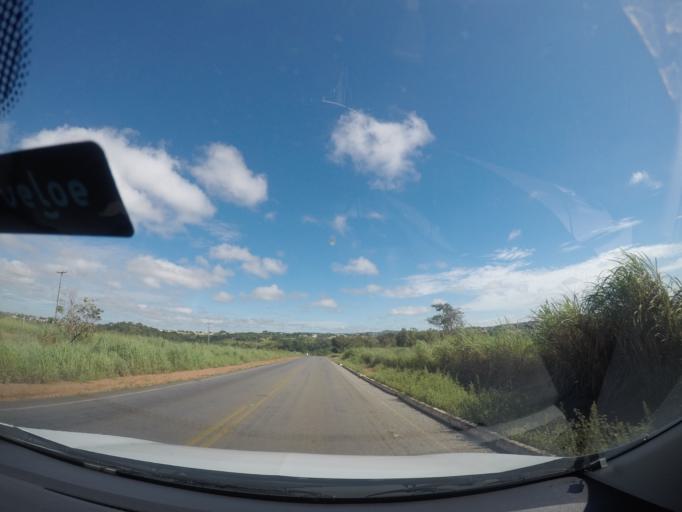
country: BR
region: Goias
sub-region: Senador Canedo
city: Senador Canedo
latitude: -16.6654
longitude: -49.1498
